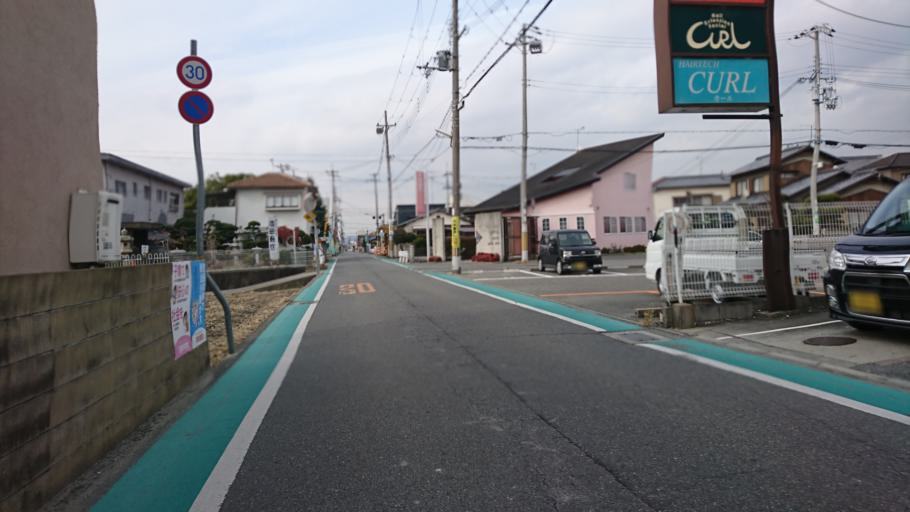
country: JP
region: Hyogo
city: Kakogawacho-honmachi
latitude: 34.7704
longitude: 134.8506
